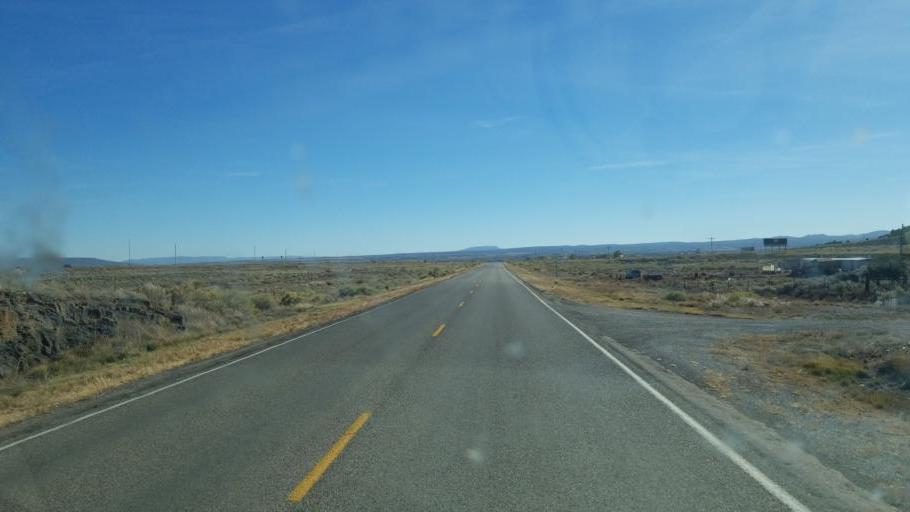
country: US
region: New Mexico
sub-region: Cibola County
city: Milan
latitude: 35.3047
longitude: -107.9879
